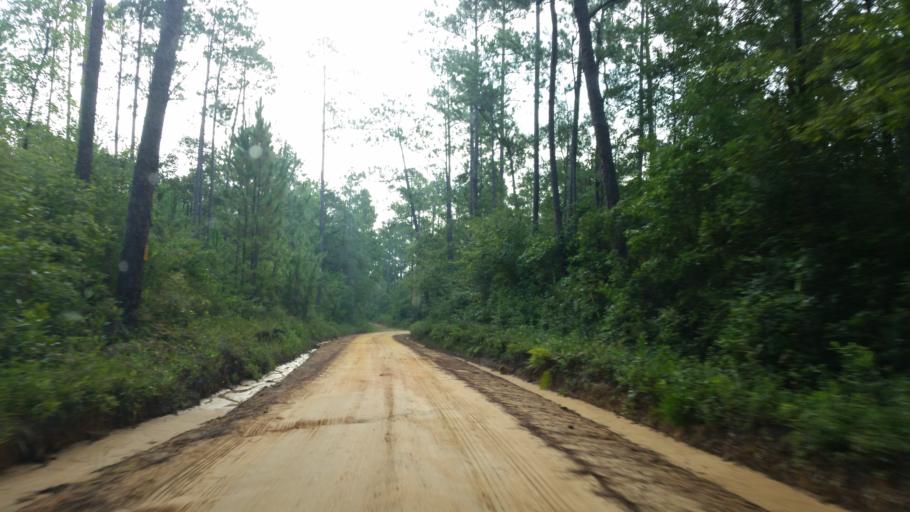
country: US
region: Alabama
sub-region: Escambia County
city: Atmore
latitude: 30.7964
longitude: -87.5540
